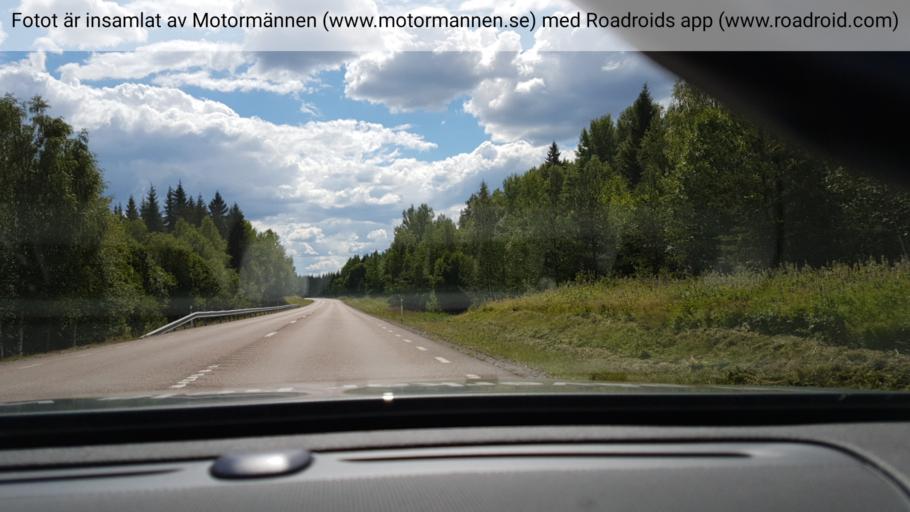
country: SE
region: Dalarna
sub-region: Faluns Kommun
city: Falun
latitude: 60.6573
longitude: 15.5537
